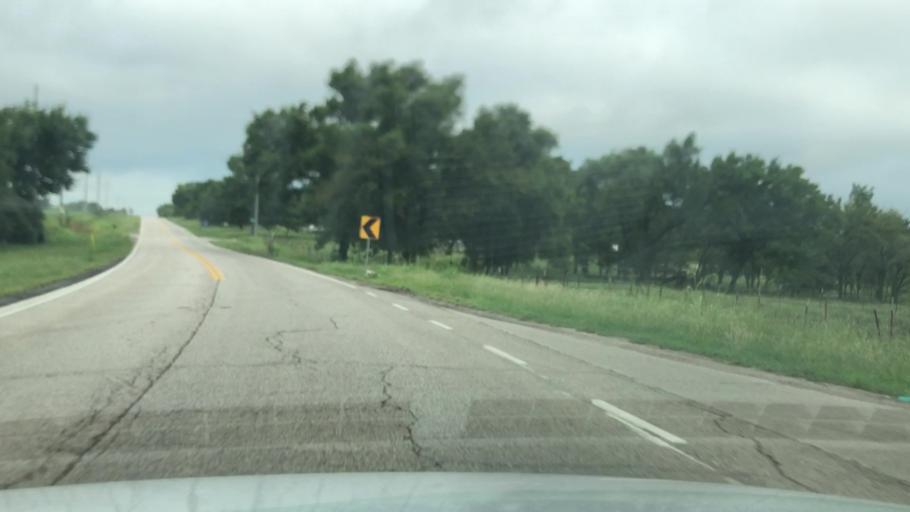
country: US
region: Oklahoma
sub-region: Nowata County
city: Nowata
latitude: 36.7136
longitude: -95.6645
